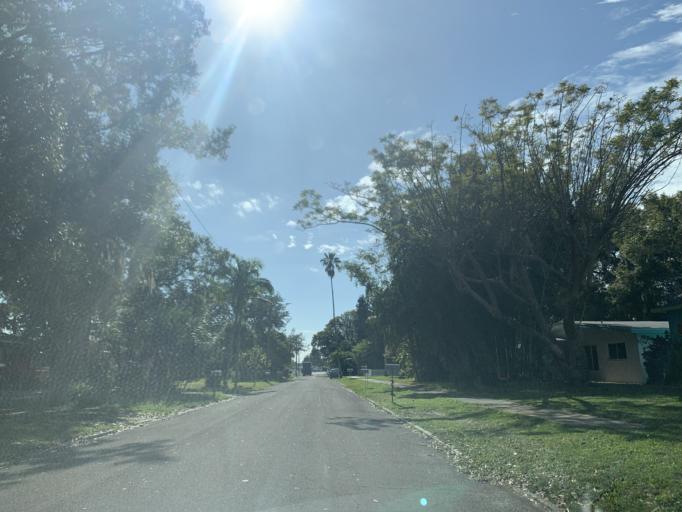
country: US
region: Florida
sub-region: Pinellas County
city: Gulfport
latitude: 27.7428
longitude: -82.6956
